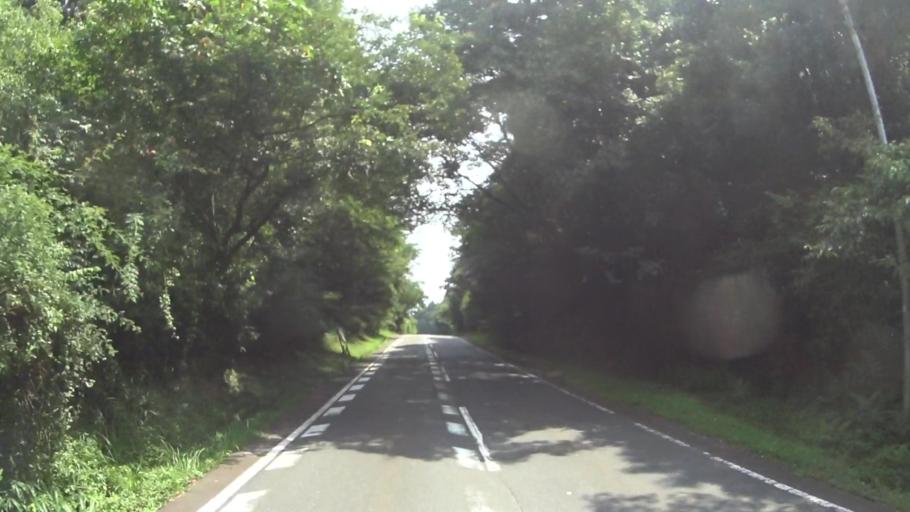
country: JP
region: Kyoto
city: Ayabe
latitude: 35.2010
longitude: 135.3706
